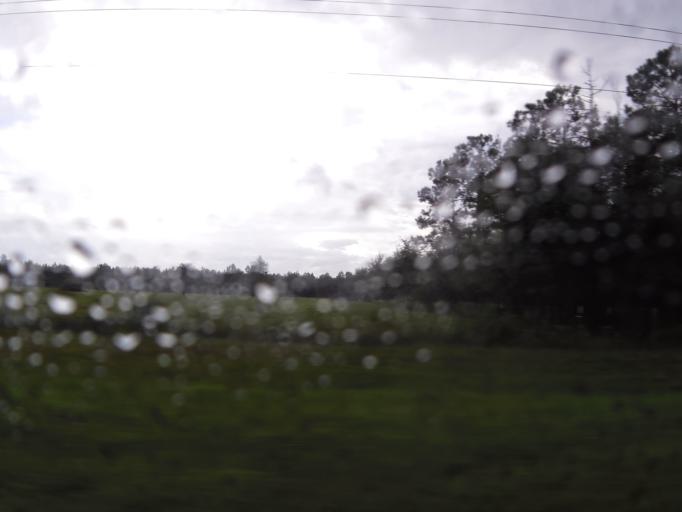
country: US
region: Florida
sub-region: Nassau County
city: Callahan
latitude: 30.5243
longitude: -81.9977
